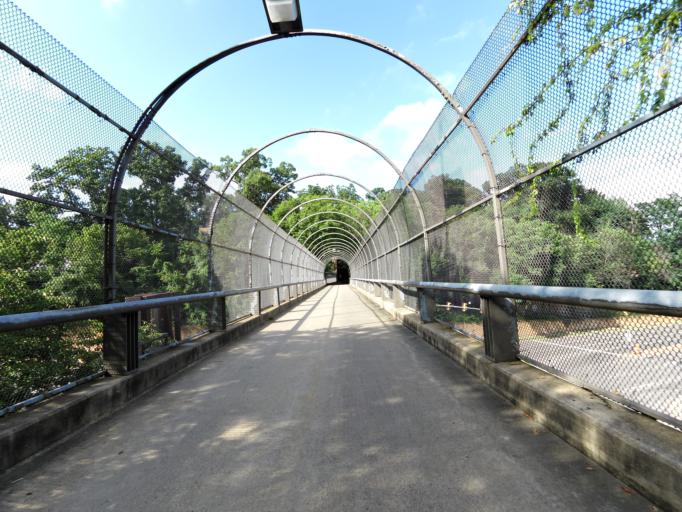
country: US
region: Virginia
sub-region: Arlington County
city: Arlington
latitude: 38.8960
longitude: -77.1002
